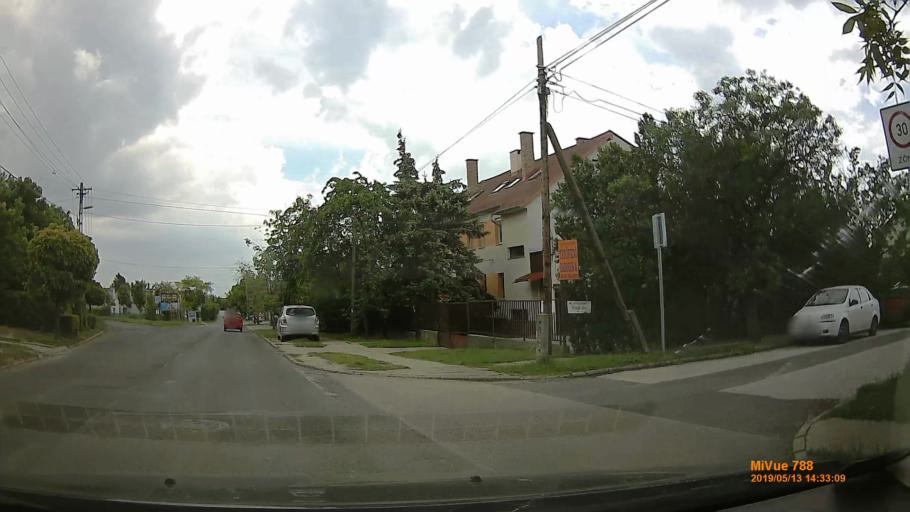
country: HU
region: Budapest
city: Budapest XXII. keruelet
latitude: 47.4255
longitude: 19.0102
